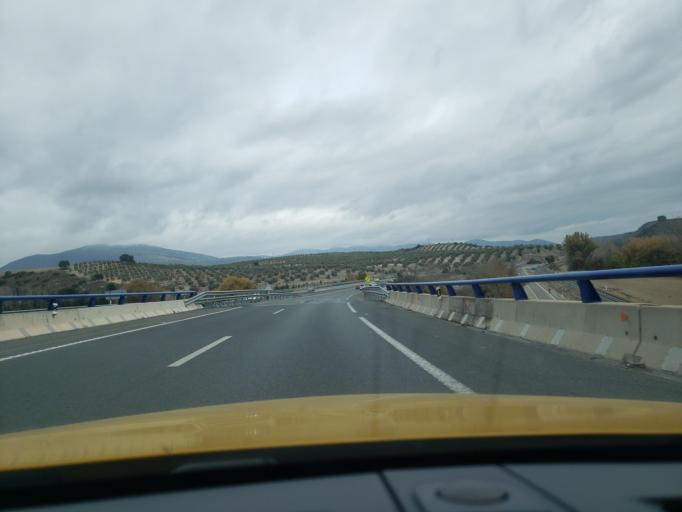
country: ES
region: Andalusia
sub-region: Provincia de Granada
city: Calicasas
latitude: 37.3030
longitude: -3.6585
